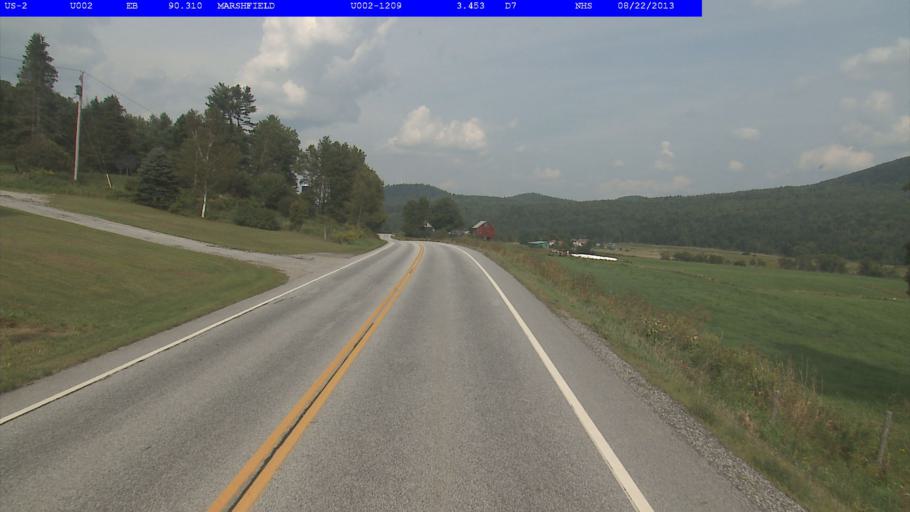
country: US
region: Vermont
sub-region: Washington County
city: Barre
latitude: 44.3167
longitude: -72.3871
